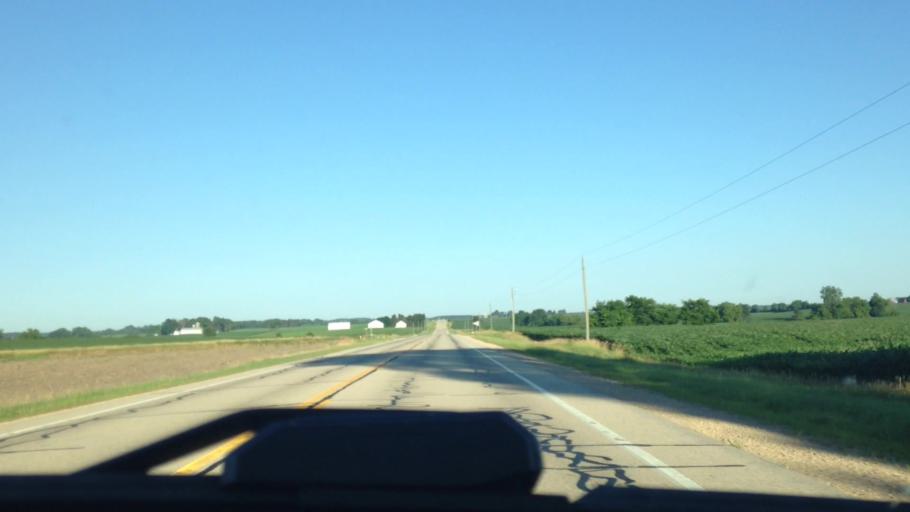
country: US
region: Wisconsin
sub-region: Columbia County
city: Rio
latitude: 43.3408
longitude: -89.2003
